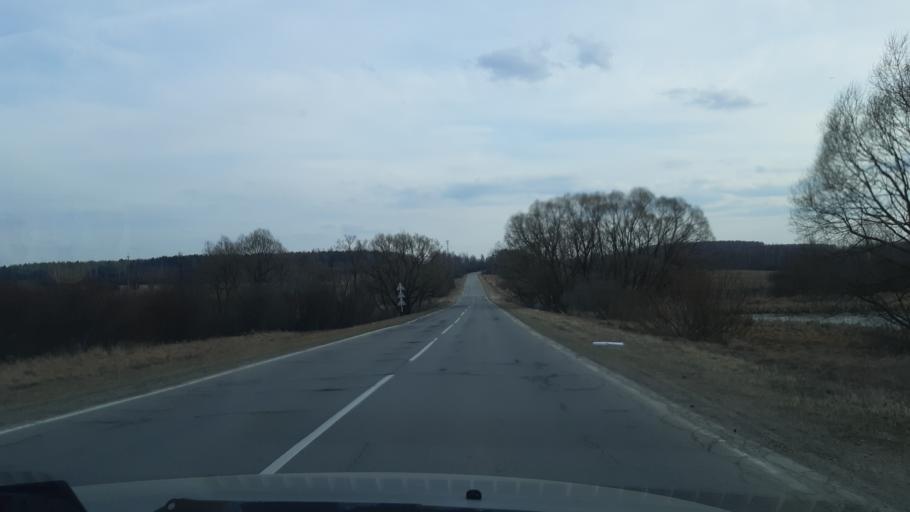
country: RU
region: Vladimir
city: Luknovo
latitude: 56.2132
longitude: 42.0309
